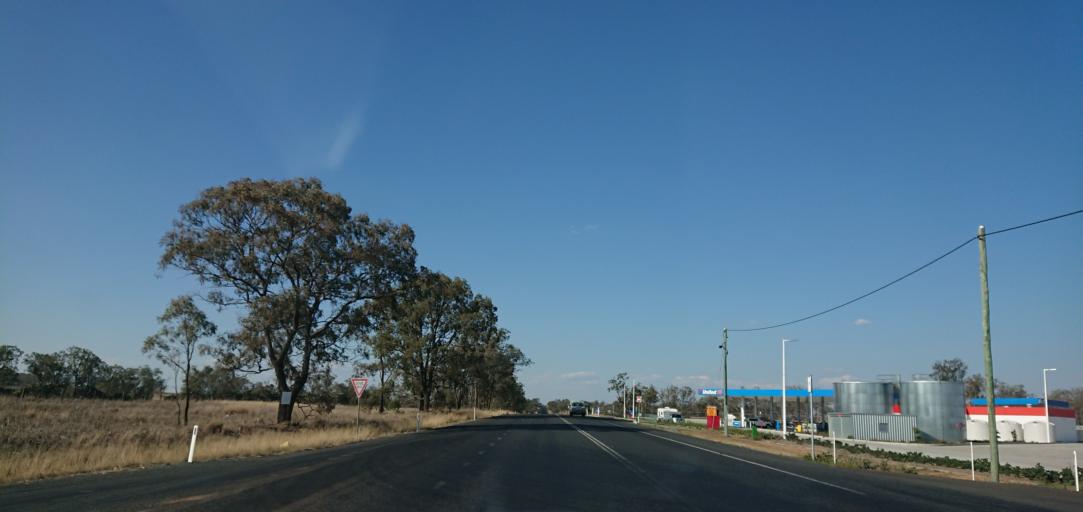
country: AU
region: Queensland
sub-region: Toowoomba
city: Westbrook
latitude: -27.6372
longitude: 151.7427
